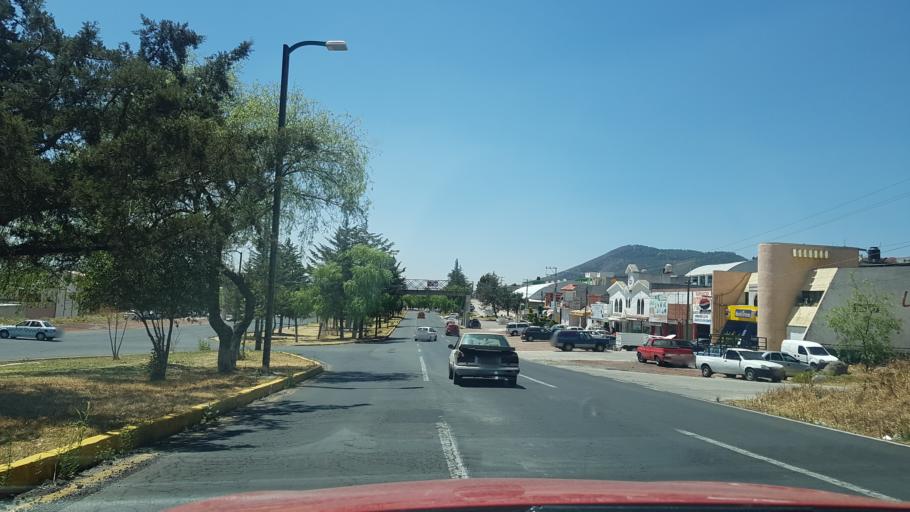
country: MX
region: Mexico
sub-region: Atlacomulco
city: Santa Cruz Bombatevi
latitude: 19.8022
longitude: -99.8856
